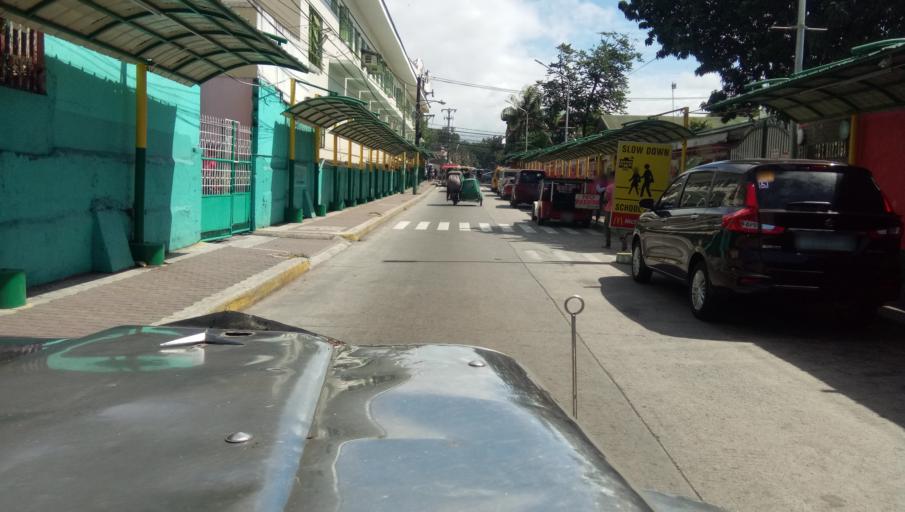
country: PH
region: Calabarzon
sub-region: Province of Cavite
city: Dasmarinas
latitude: 14.3269
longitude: 120.9348
